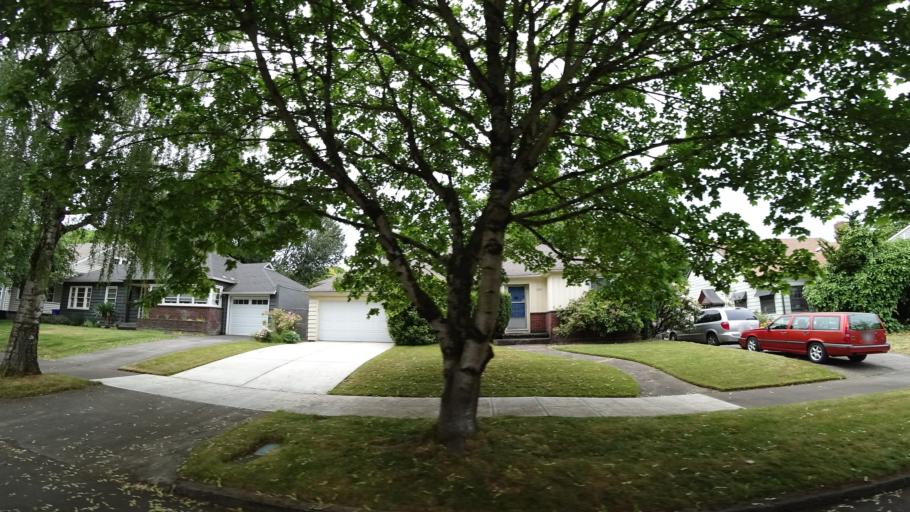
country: US
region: Oregon
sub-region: Multnomah County
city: Portland
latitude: 45.5765
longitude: -122.7059
